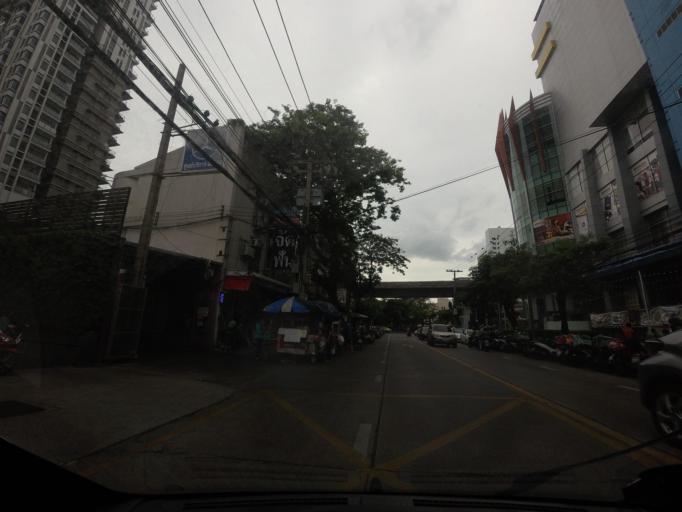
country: TH
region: Bangkok
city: Ratchathewi
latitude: 13.7611
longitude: 100.5372
